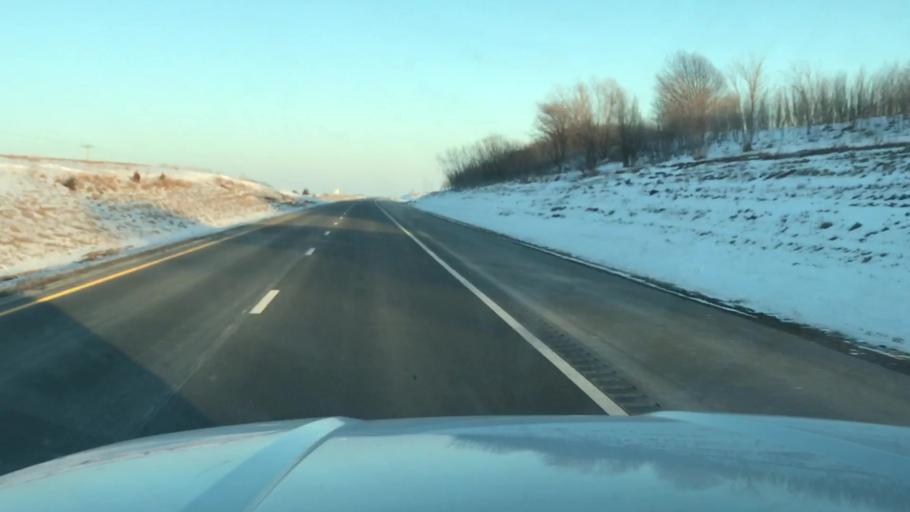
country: US
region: Missouri
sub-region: Clinton County
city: Gower
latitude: 39.7619
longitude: -94.5294
